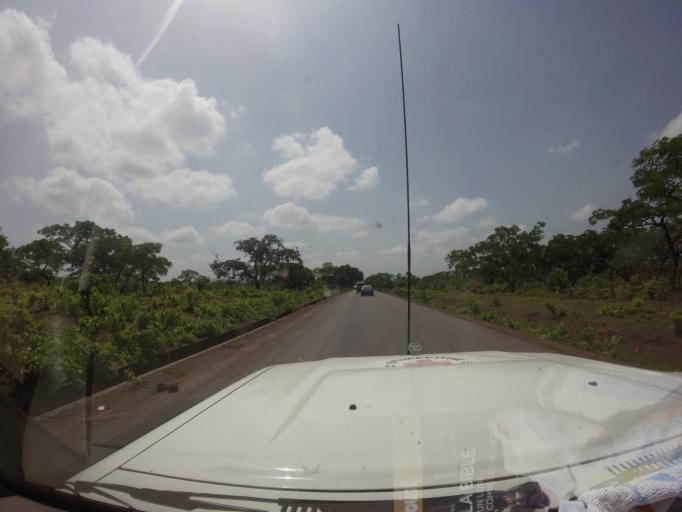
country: GN
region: Mamou
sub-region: Mamou Prefecture
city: Mamou
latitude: 10.2938
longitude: -12.3535
